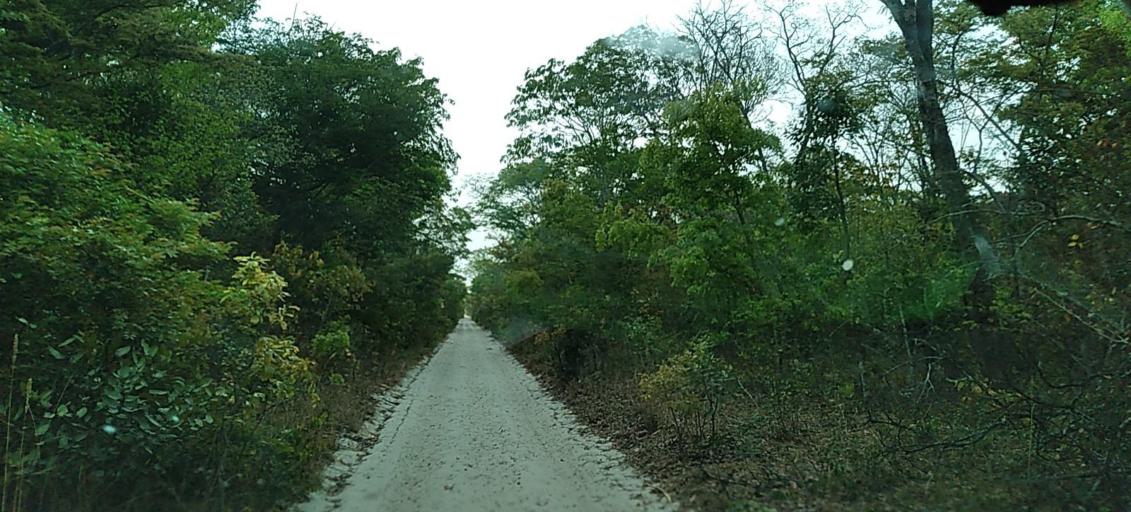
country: ZM
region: North-Western
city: Kabompo
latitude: -13.3985
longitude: 23.8060
